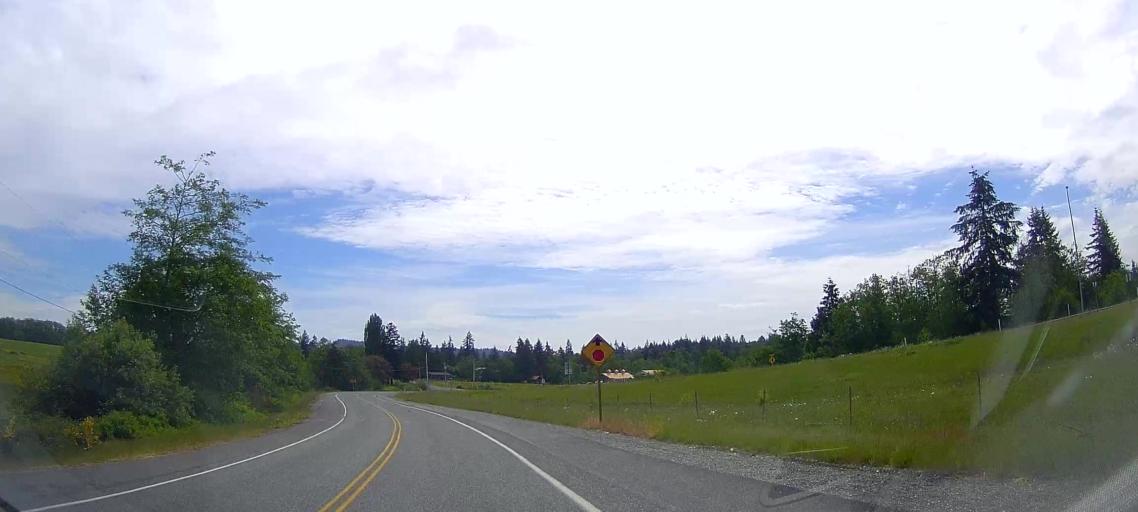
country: US
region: Washington
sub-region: Snohomish County
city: Stanwood
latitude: 48.3105
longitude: -122.3159
